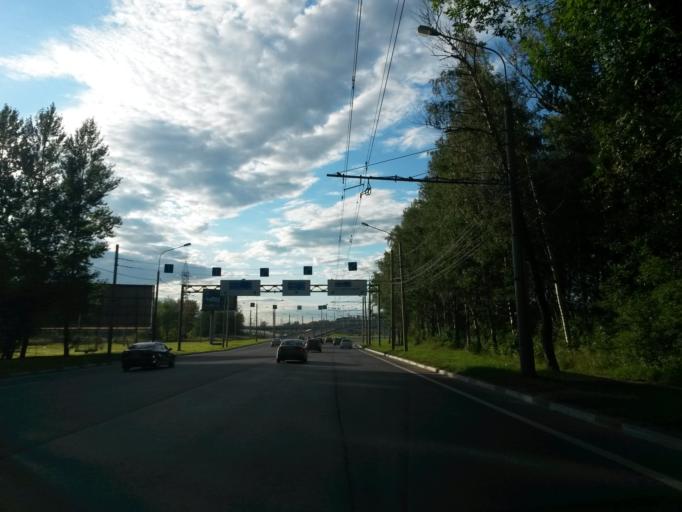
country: RU
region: Jaroslavl
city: Yaroslavl
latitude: 57.6650
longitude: 39.8445
